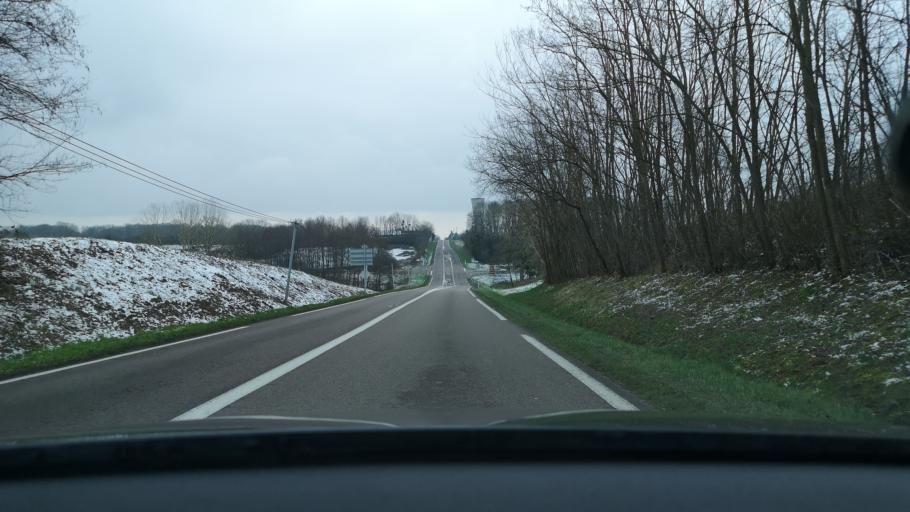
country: FR
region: Bourgogne
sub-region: Departement de Saone-et-Loire
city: Saint-Germain-du-Plain
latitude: 46.7571
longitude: 5.0054
